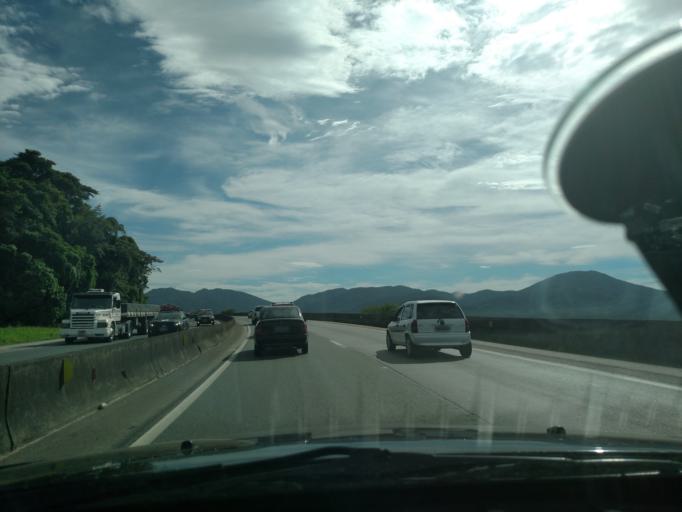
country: BR
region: Santa Catarina
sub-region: Biguacu
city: Biguacu
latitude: -27.4338
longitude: -48.6253
